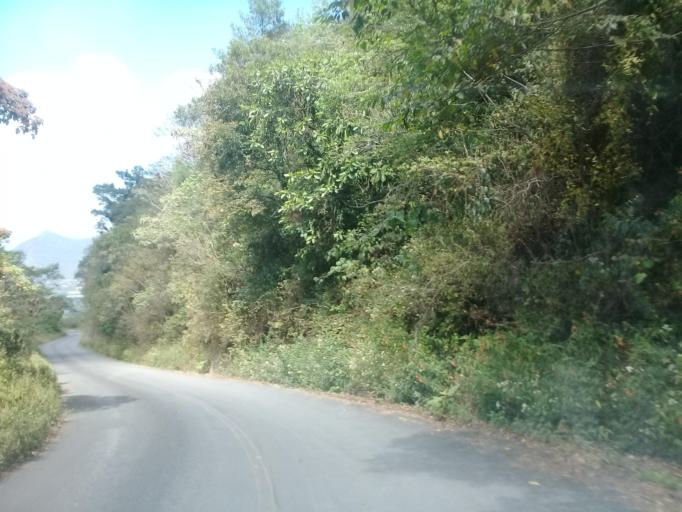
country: MX
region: Veracruz
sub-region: Tlilapan
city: Tonalixco
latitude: 18.8105
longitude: -97.0608
